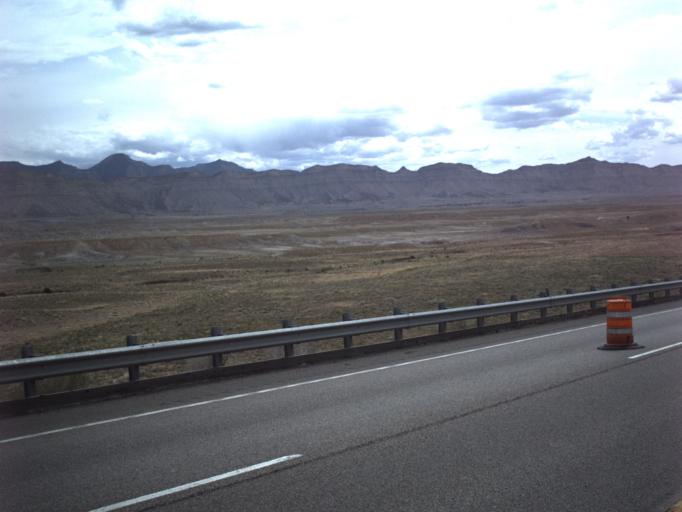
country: US
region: Utah
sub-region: Carbon County
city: East Carbon City
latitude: 39.3924
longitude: -110.4163
